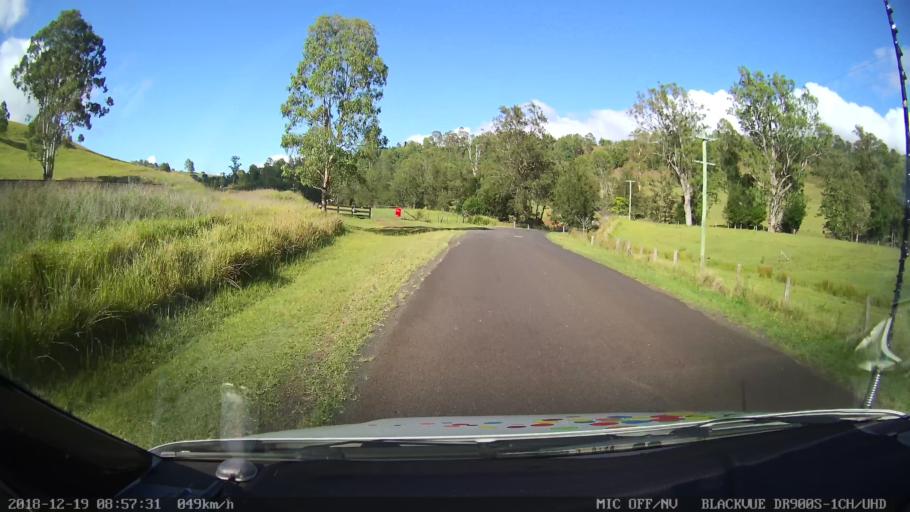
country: AU
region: New South Wales
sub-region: Kyogle
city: Kyogle
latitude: -28.4211
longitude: 152.9712
